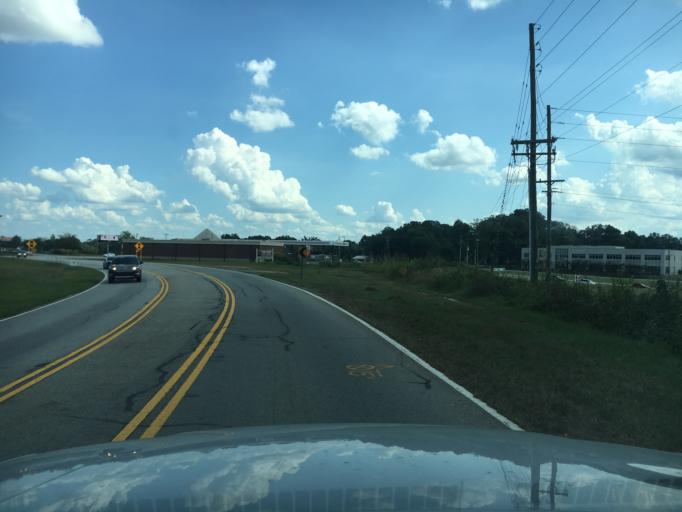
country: US
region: South Carolina
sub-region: Pickens County
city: Clemson
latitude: 34.6977
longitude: -82.8797
